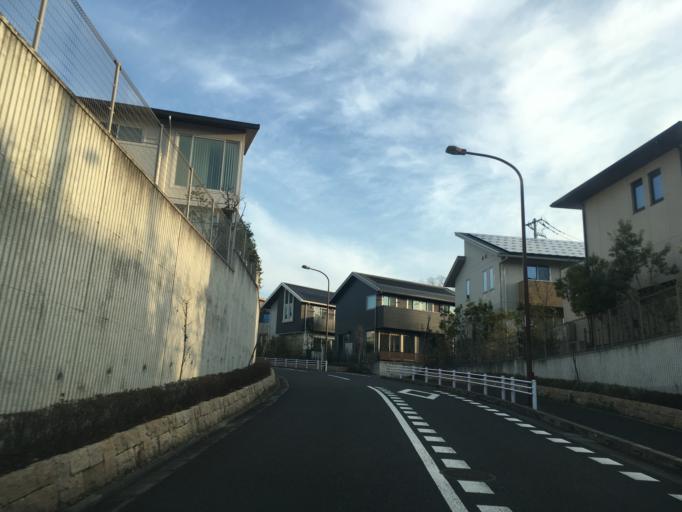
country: JP
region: Tokyo
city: Hino
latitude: 35.6331
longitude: 139.4001
